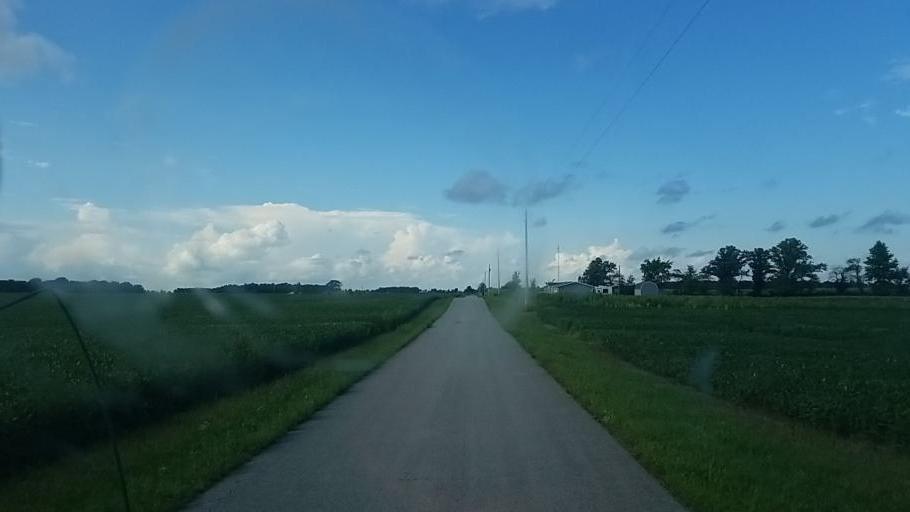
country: US
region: Ohio
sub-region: Hardin County
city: Forest
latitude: 40.7684
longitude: -83.4487
